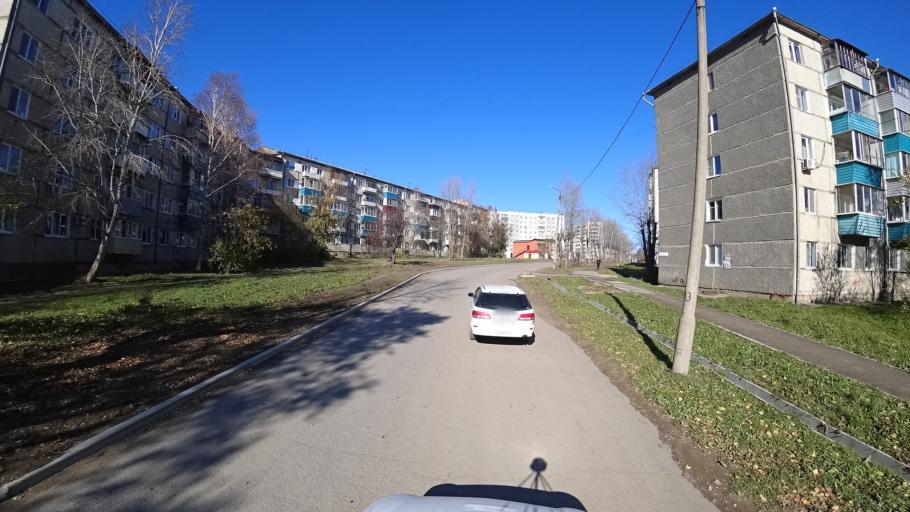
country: RU
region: Khabarovsk Krai
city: Amursk
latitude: 50.2164
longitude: 136.8926
